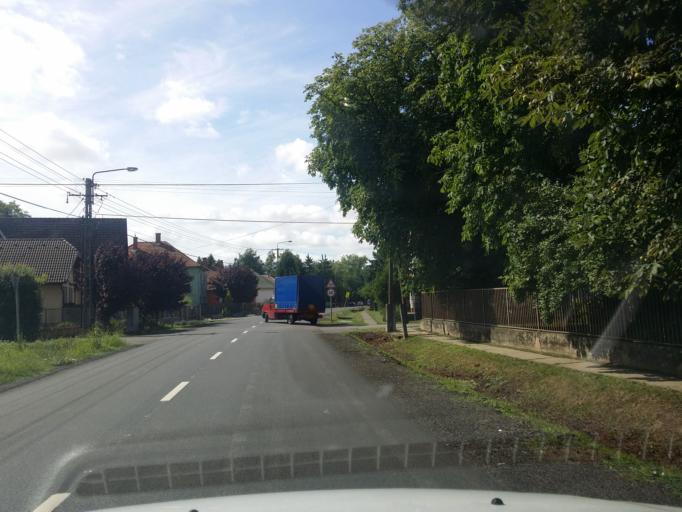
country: HU
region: Heves
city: Heves
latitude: 47.6048
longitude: 20.2872
